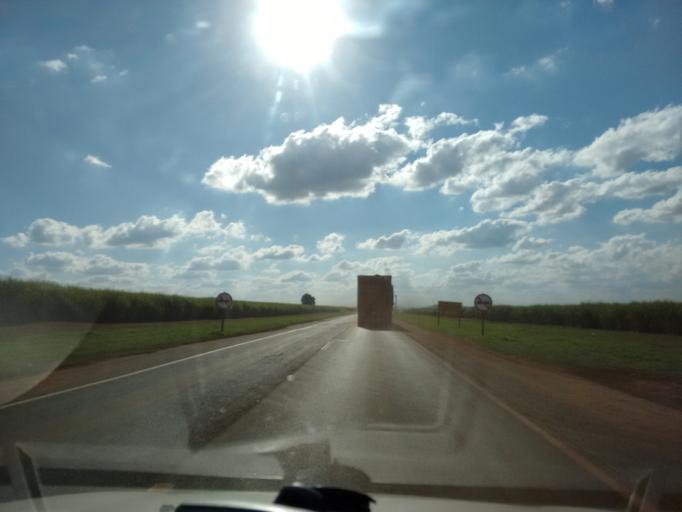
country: BR
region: Sao Paulo
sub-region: Americo Brasiliense
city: Americo Brasiliense
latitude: -21.6163
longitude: -48.0286
